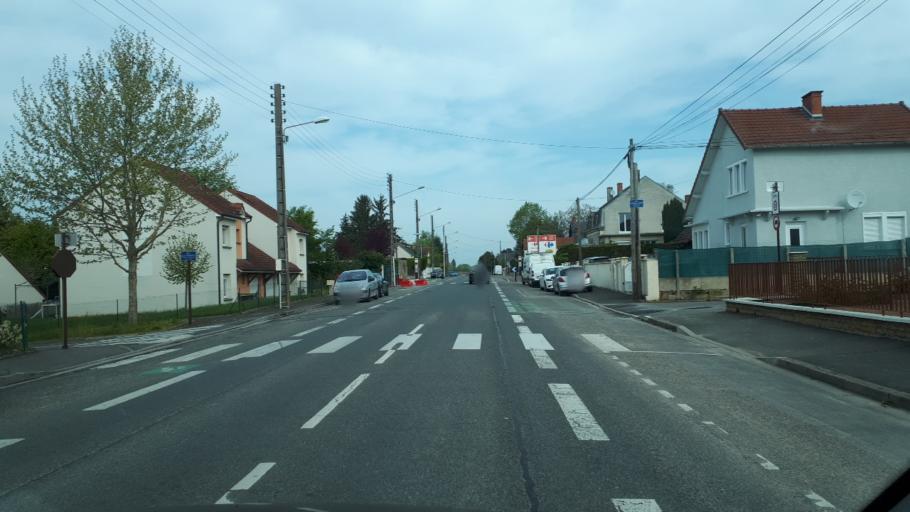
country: FR
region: Centre
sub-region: Departement du Cher
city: Bourges
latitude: 47.0612
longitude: 2.4235
